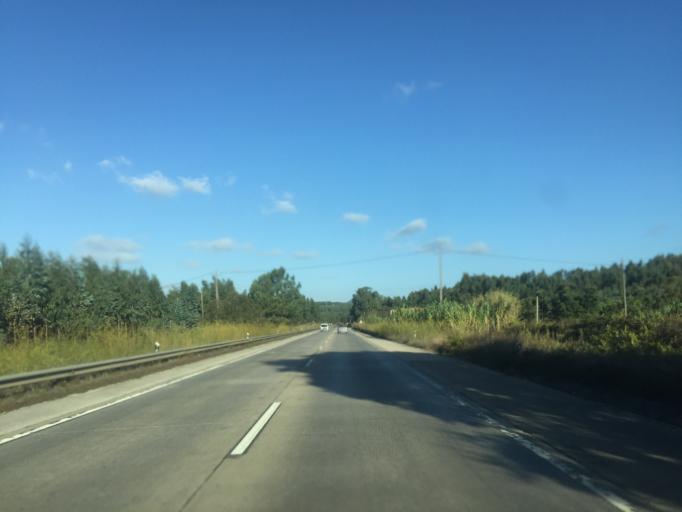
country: PT
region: Santarem
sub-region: Rio Maior
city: Rio Maior
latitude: 39.2881
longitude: -8.9437
